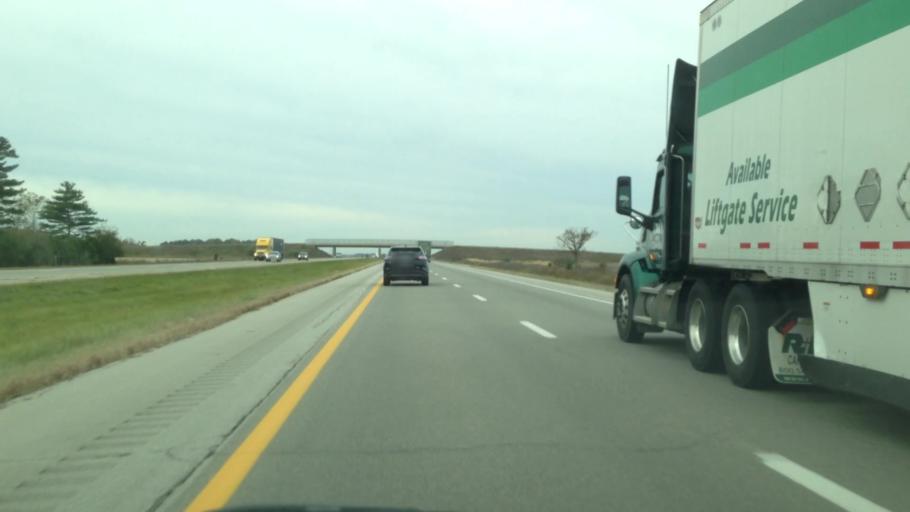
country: US
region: Ohio
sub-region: Fulton County
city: Burlington
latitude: 41.5908
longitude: -84.2247
